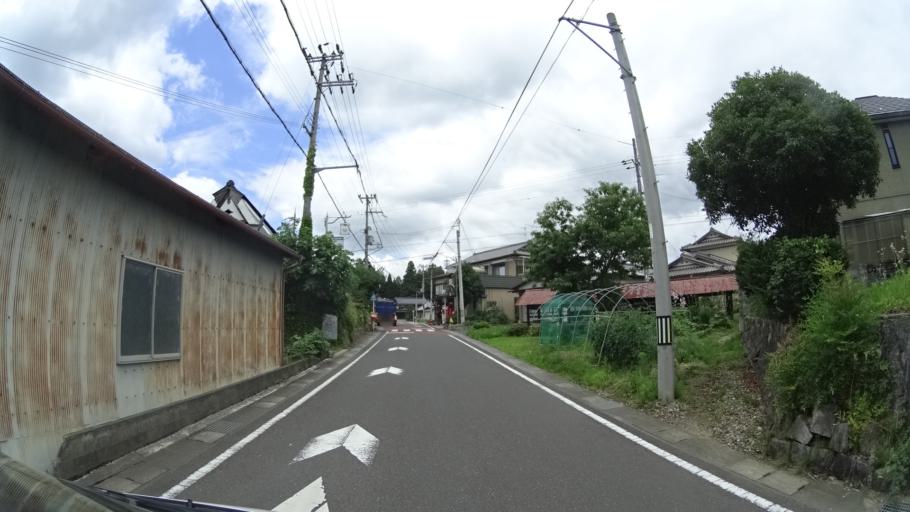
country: JP
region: Kyoto
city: Ayabe
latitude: 35.3195
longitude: 135.2703
